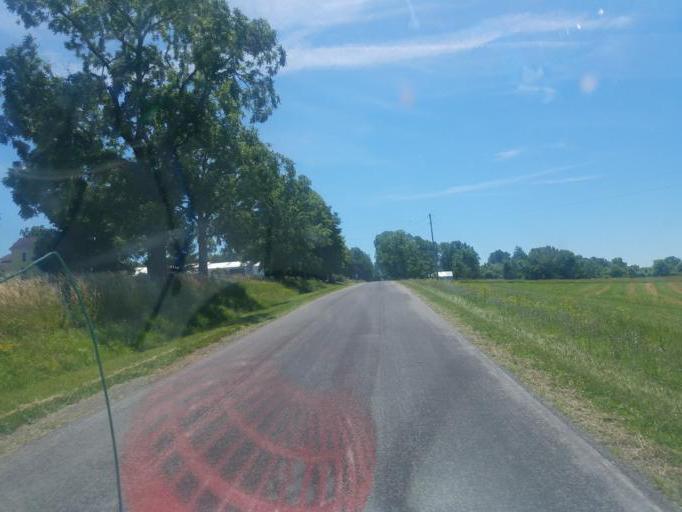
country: US
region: New York
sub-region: Yates County
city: Penn Yan
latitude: 42.6387
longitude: -77.0162
